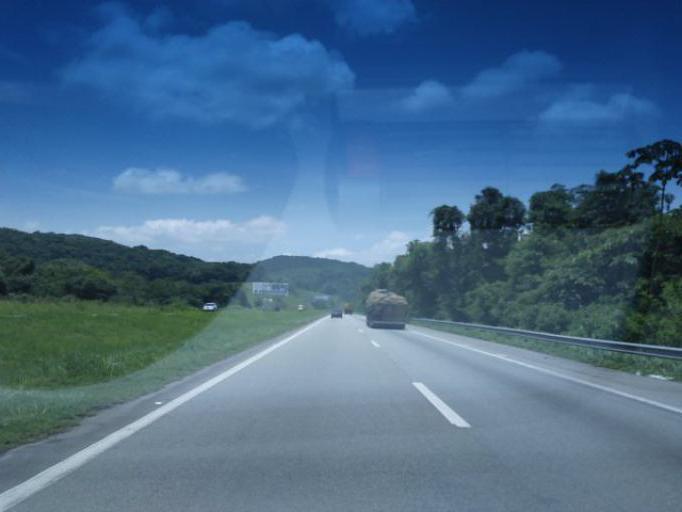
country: BR
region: Sao Paulo
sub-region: Miracatu
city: Miracatu
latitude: -24.2134
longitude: -47.3691
